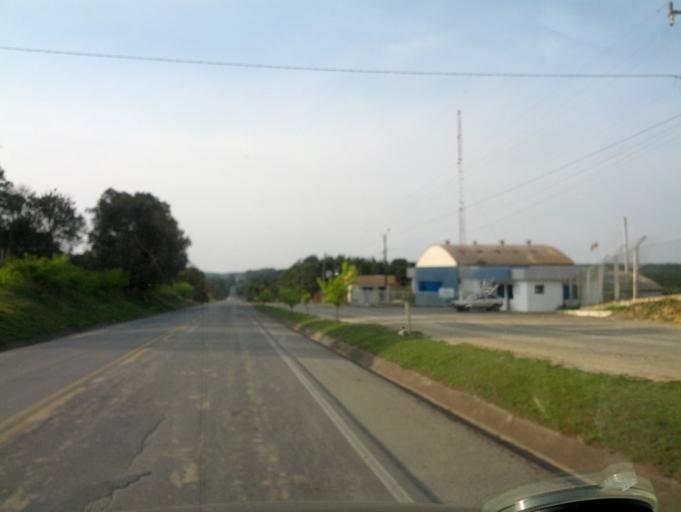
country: BR
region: Santa Catarina
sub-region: Otacilio Costa
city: Otacilio Costa
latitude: -27.5988
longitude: -50.1714
